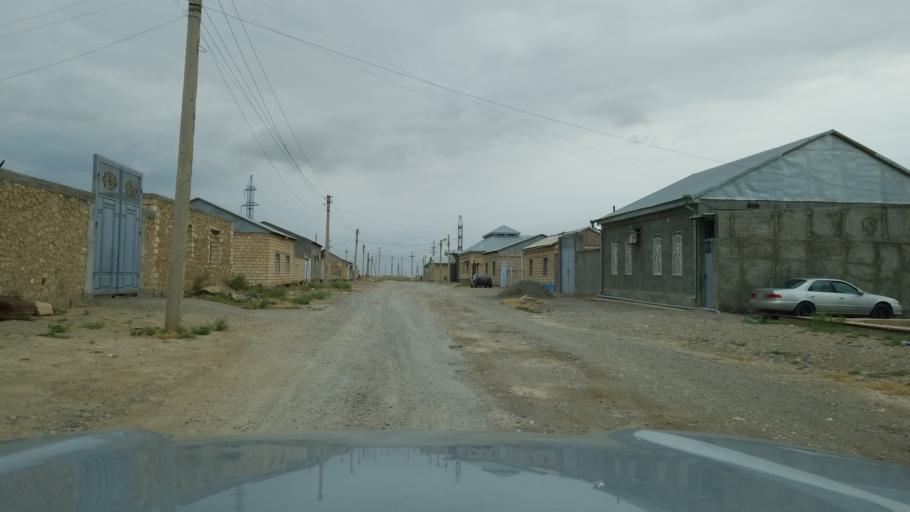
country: TM
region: Balkan
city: Serdar
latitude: 38.9678
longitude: 56.2616
